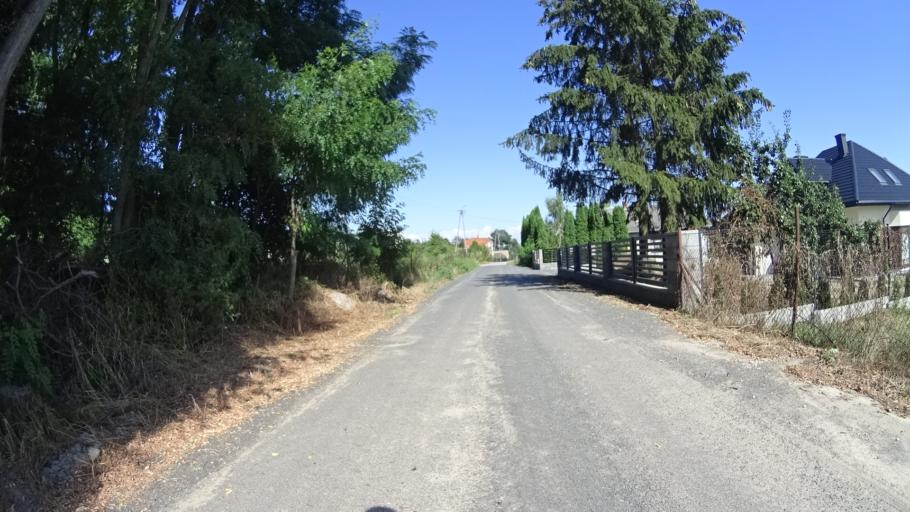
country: PL
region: Masovian Voivodeship
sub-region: Powiat bialobrzeski
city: Promna
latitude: 51.6700
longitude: 20.9351
